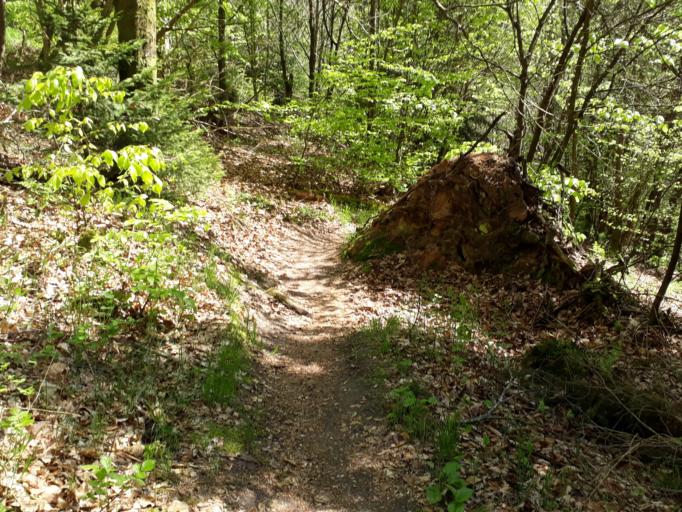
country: FR
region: Alsace
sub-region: Departement du Bas-Rhin
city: Neuwiller-les-Saverne
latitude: 48.8461
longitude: 7.3138
